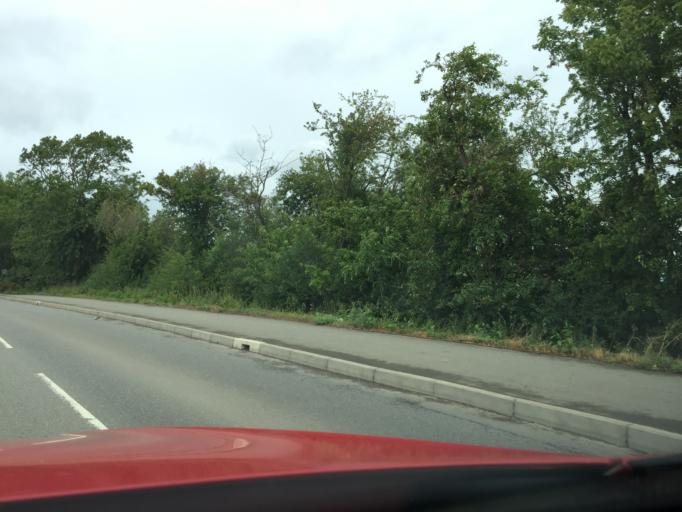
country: GB
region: England
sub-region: Warwickshire
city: Southam
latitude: 52.2485
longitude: -1.3782
